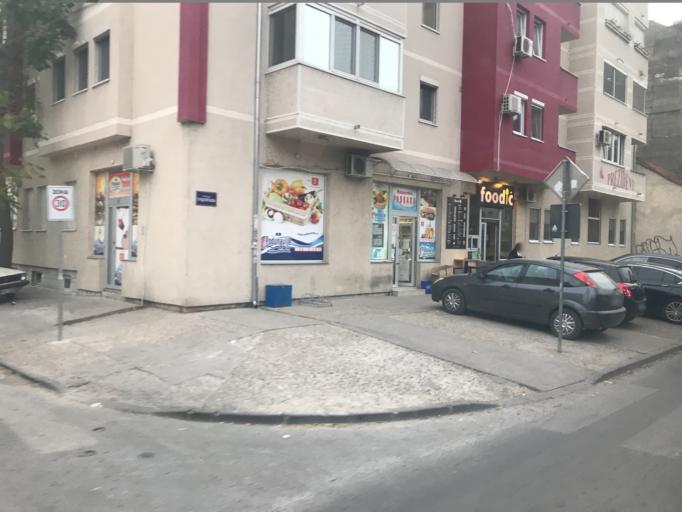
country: RS
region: Autonomna Pokrajina Vojvodina
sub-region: Juznobacki Okrug
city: Novi Sad
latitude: 45.2643
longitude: 19.8463
